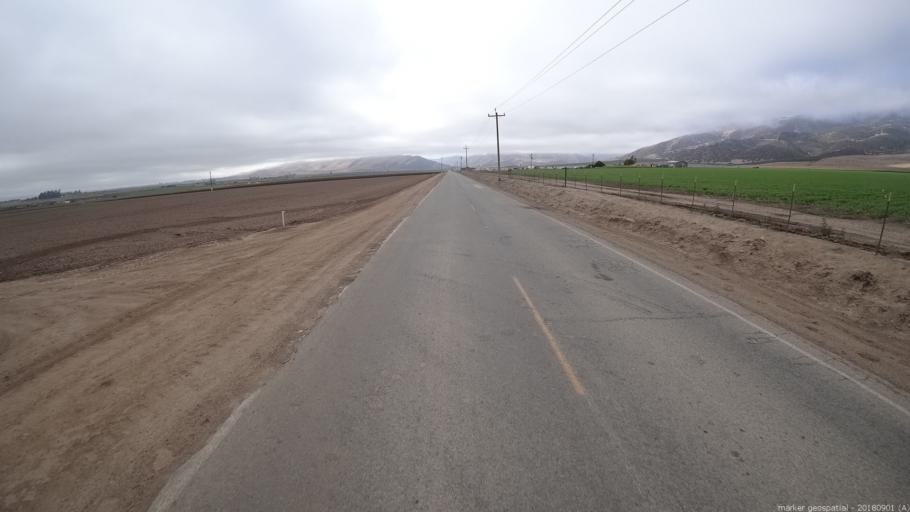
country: US
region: California
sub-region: Monterey County
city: Greenfield
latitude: 36.3305
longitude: -121.3155
